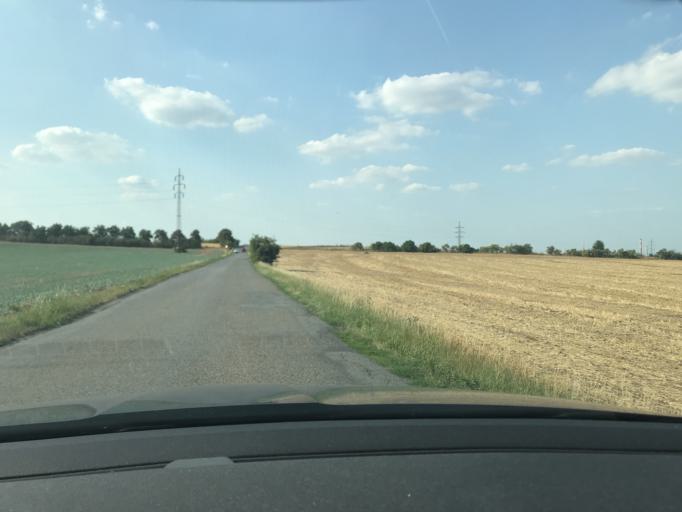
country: CZ
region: Central Bohemia
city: Kralupy nad Vltavou
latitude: 50.2244
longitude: 14.3229
